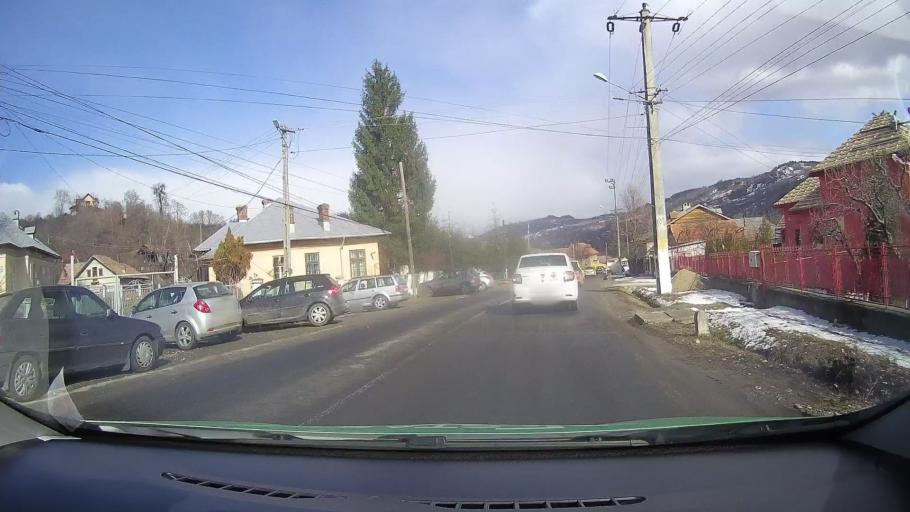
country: RO
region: Dambovita
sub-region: Comuna Pietrosita
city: Pietrosita
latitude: 45.1845
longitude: 25.4370
